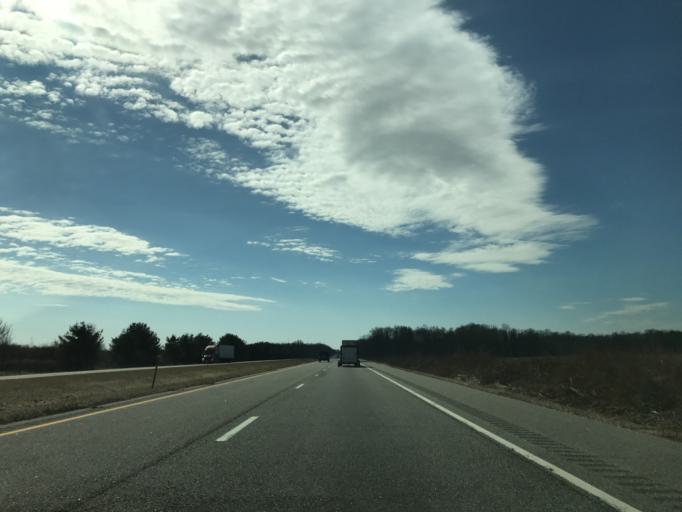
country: US
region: Delaware
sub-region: New Castle County
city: Townsend
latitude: 39.3467
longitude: -75.8280
